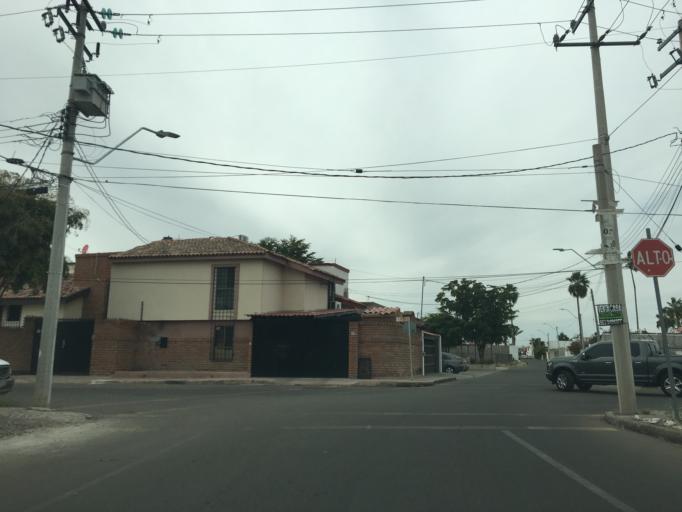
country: MX
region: Sonora
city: Hermosillo
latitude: 29.0758
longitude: -110.9680
